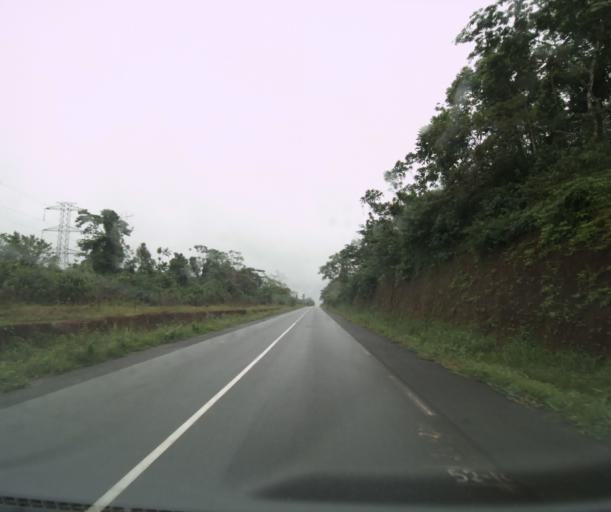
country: CM
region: Littoral
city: Dizangue
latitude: 3.3599
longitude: 10.1026
